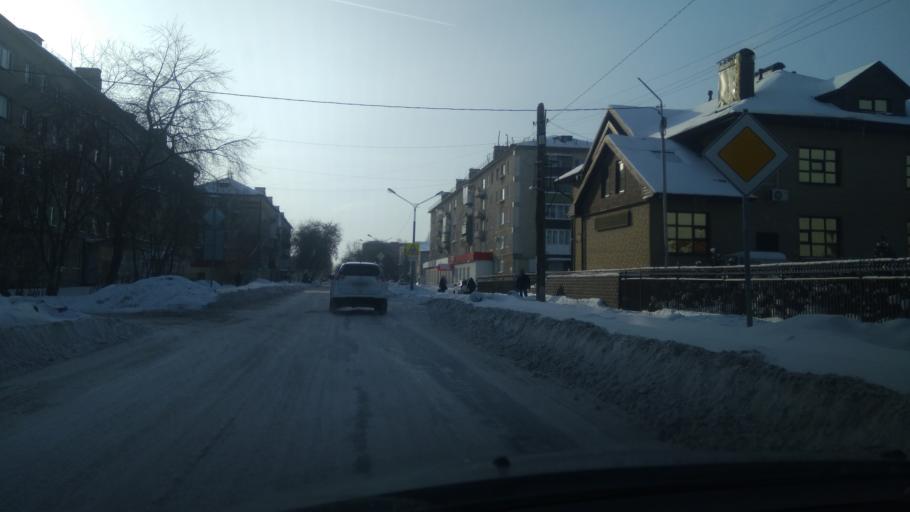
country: RU
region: Sverdlovsk
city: Sukhoy Log
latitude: 56.9045
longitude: 62.0321
